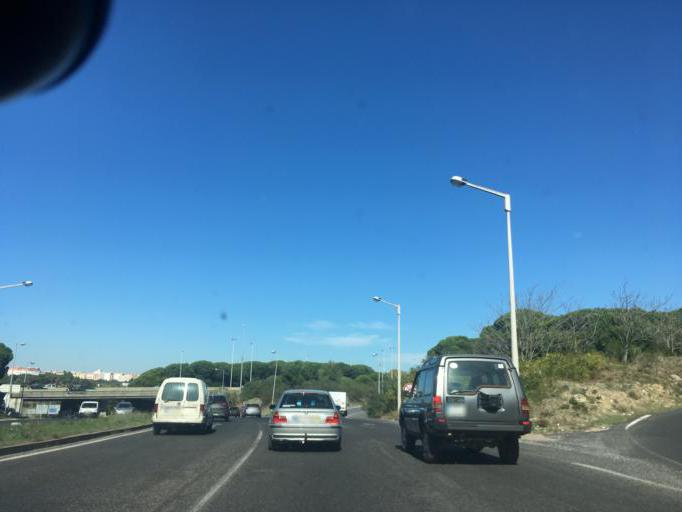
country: PT
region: Lisbon
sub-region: Oeiras
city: Alges
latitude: 38.7182
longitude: -9.2092
